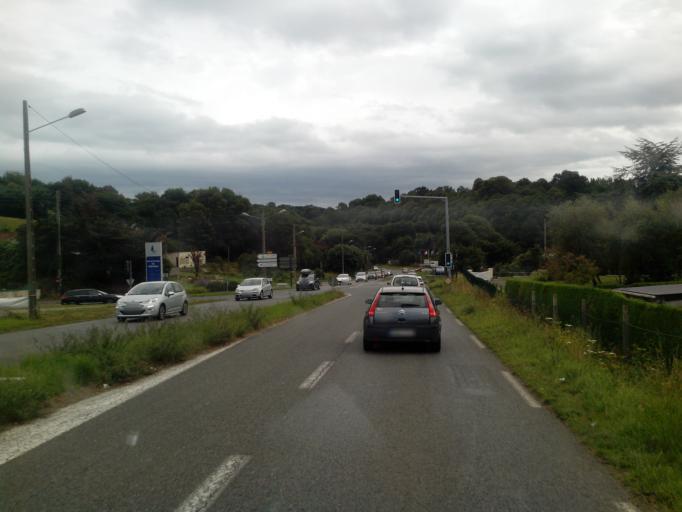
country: FR
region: Brittany
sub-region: Departement des Cotes-d'Armor
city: Etables-sur-Mer
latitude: 48.6398
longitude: -2.8357
